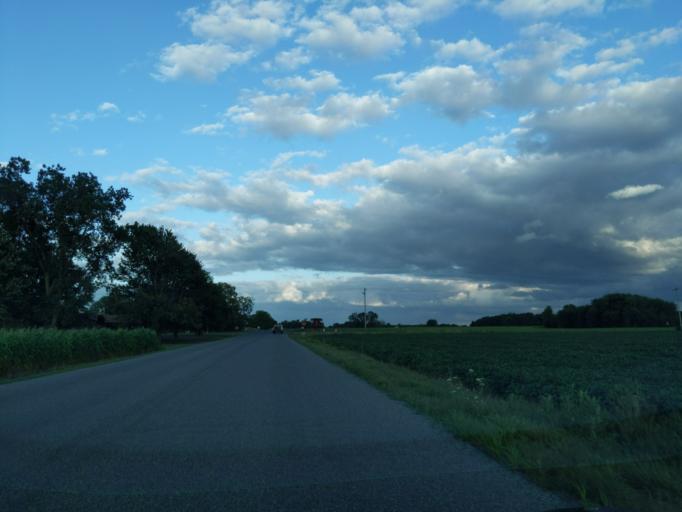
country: US
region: Michigan
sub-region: Ingham County
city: Holt
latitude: 42.5968
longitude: -84.5643
